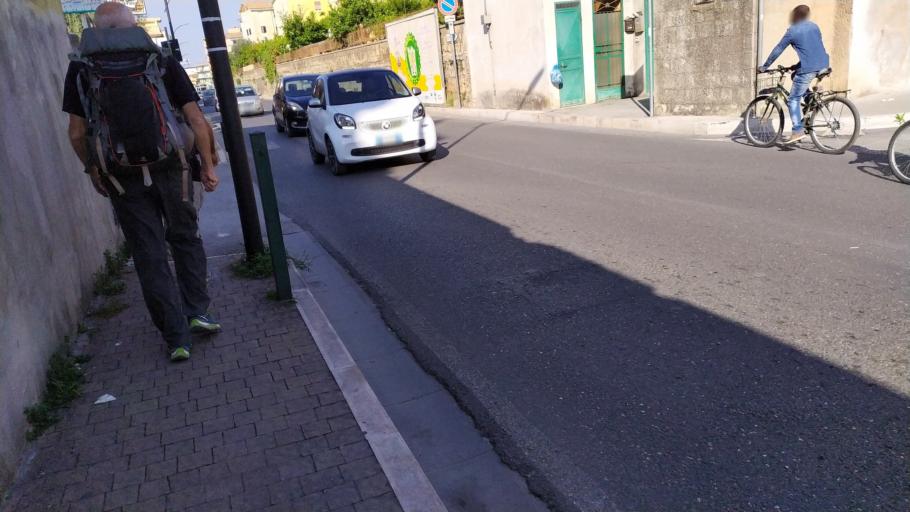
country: IT
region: Campania
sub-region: Provincia di Caserta
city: Maddaloni
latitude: 41.0347
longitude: 14.3876
